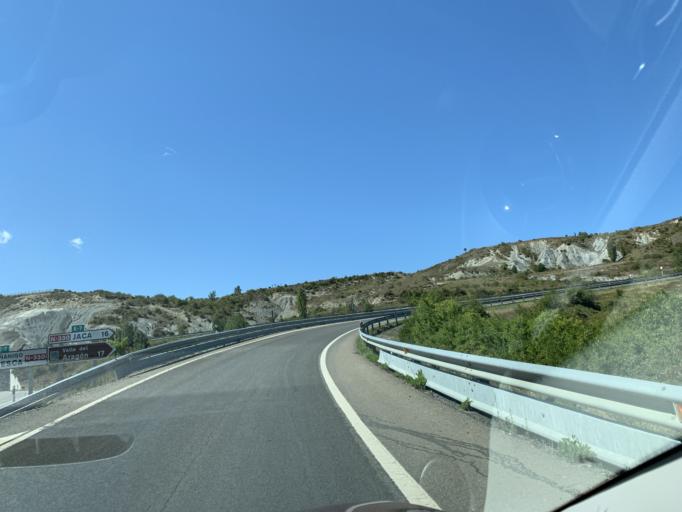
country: ES
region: Aragon
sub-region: Provincia de Huesca
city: Sabinanigo
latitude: 42.5361
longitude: -0.3703
